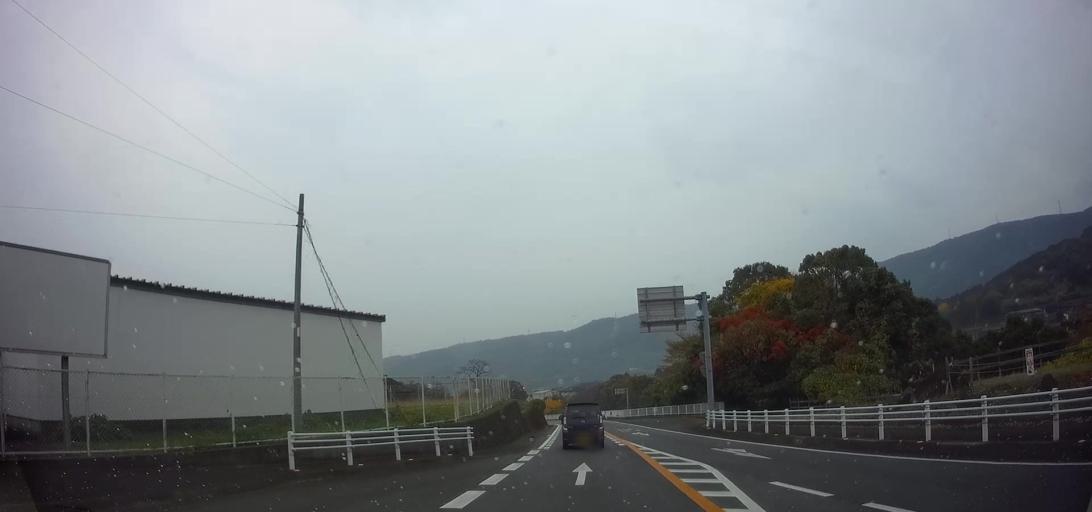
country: JP
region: Nagasaki
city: Shimabara
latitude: 32.7826
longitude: 130.2054
